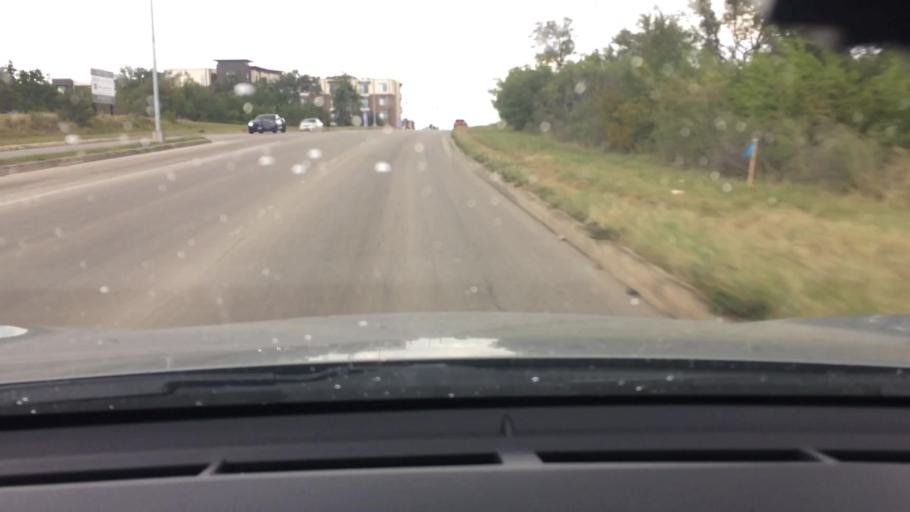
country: US
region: Texas
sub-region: Bexar County
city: Shavano Park
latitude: 29.5872
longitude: -98.5888
